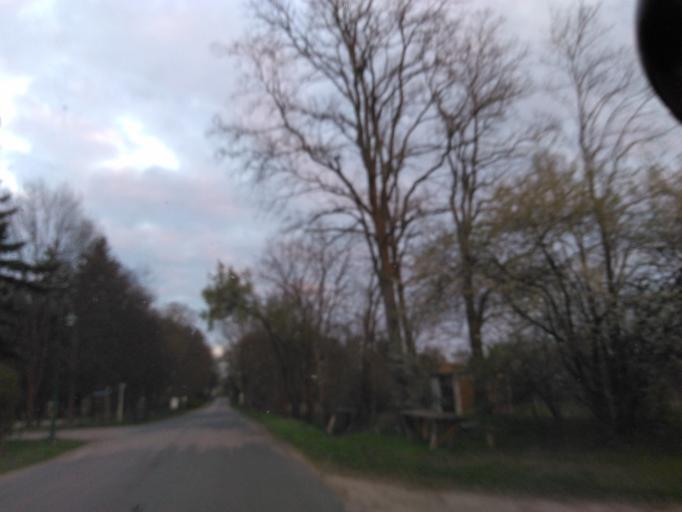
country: DE
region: Brandenburg
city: Protzel
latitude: 52.6494
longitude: 14.0667
